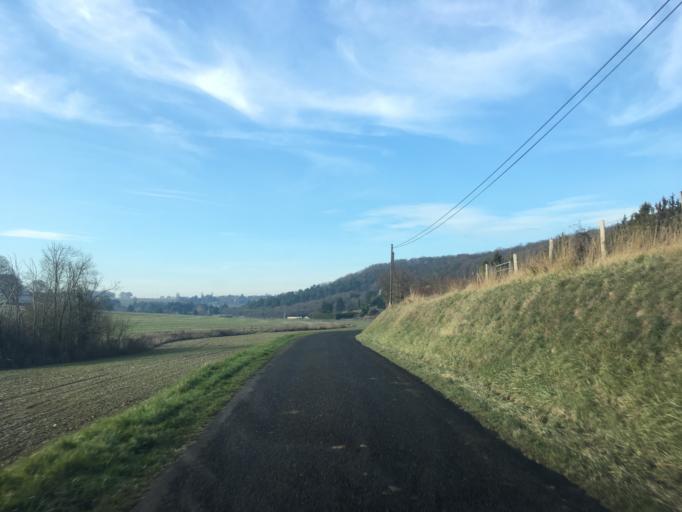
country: FR
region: Haute-Normandie
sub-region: Departement de l'Eure
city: Menilles
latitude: 49.0474
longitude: 1.2844
